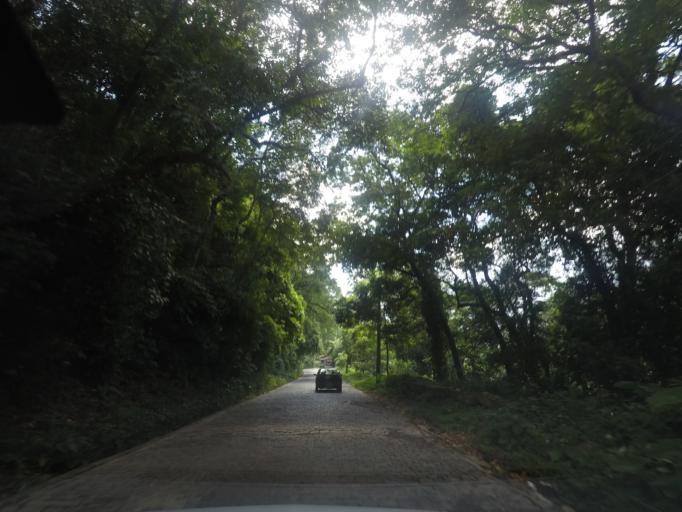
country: BR
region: Rio de Janeiro
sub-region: Petropolis
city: Petropolis
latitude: -22.5433
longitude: -43.1819
